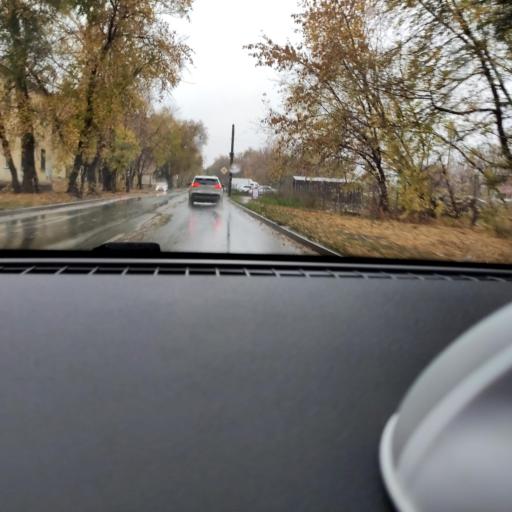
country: RU
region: Samara
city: Samara
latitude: 53.2165
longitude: 50.1941
